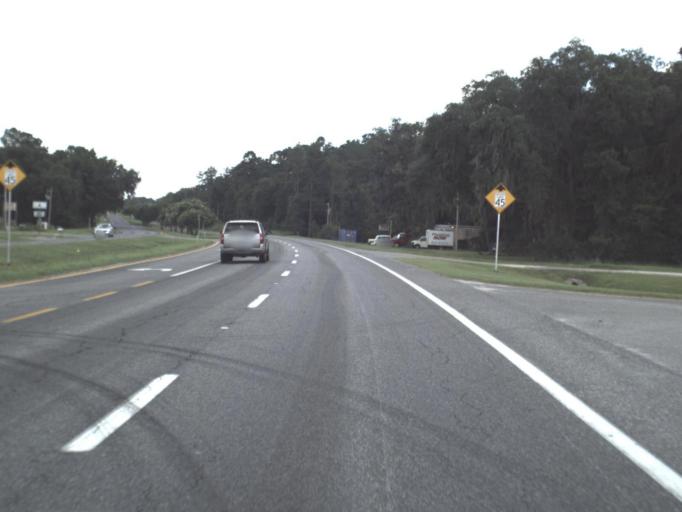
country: US
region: Florida
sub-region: Columbia County
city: Lake City
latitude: 30.1518
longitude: -82.6432
